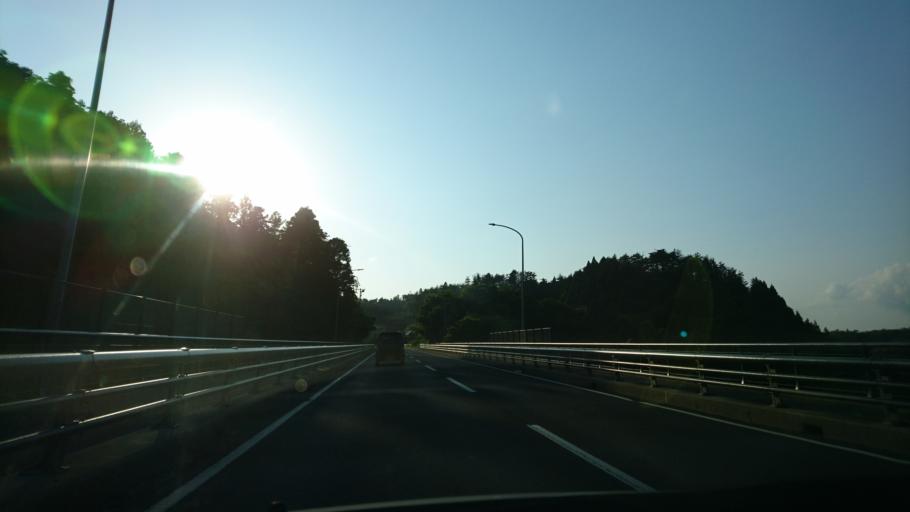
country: JP
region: Iwate
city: Ofunato
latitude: 38.9151
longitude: 141.5239
